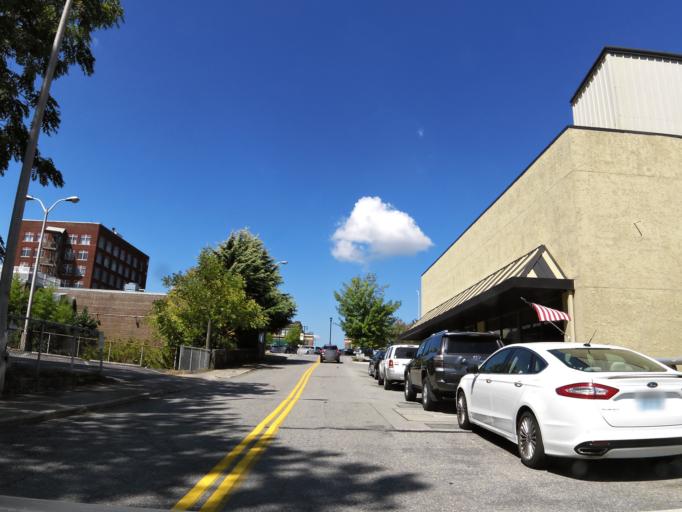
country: US
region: Tennessee
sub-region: Blount County
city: Maryville
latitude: 35.7563
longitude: -83.9690
